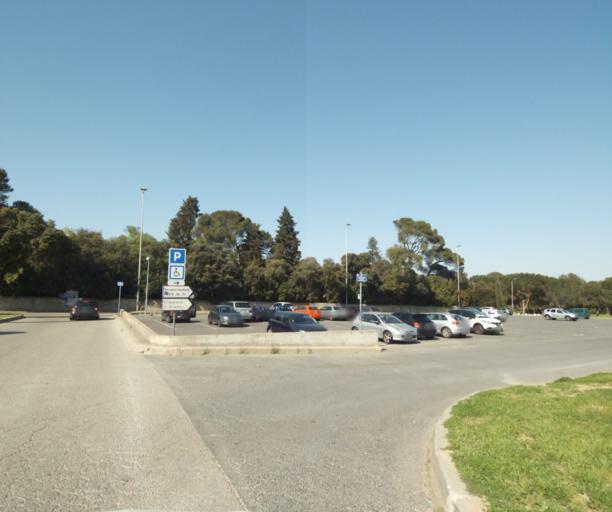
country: FR
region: Languedoc-Roussillon
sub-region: Departement de l'Herault
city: Le Cres
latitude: 43.6143
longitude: 3.9302
